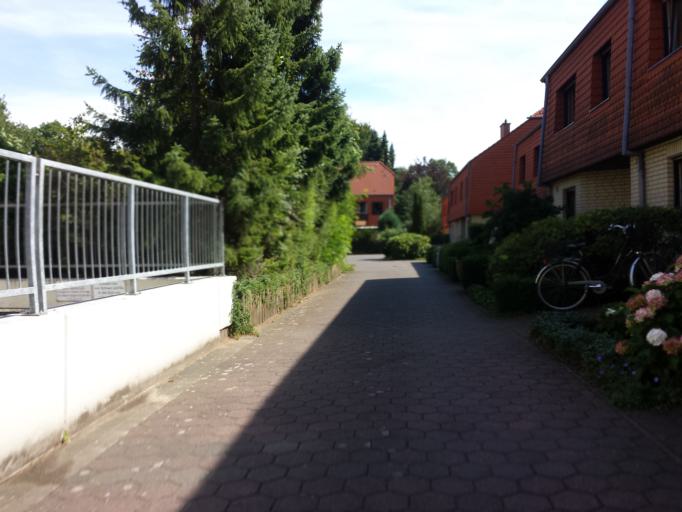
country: DE
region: North Rhine-Westphalia
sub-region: Regierungsbezirk Detmold
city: Guetersloh
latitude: 51.8941
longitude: 8.3753
